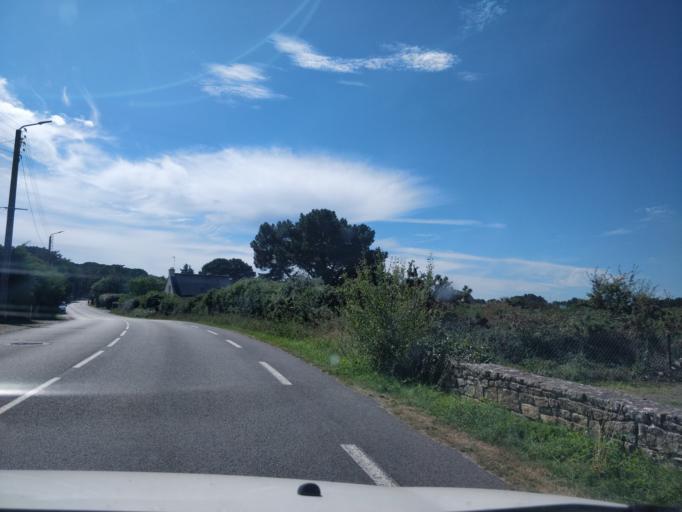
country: FR
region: Brittany
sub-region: Departement du Morbihan
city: Saint-Philibert
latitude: 47.5744
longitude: -3.0004
